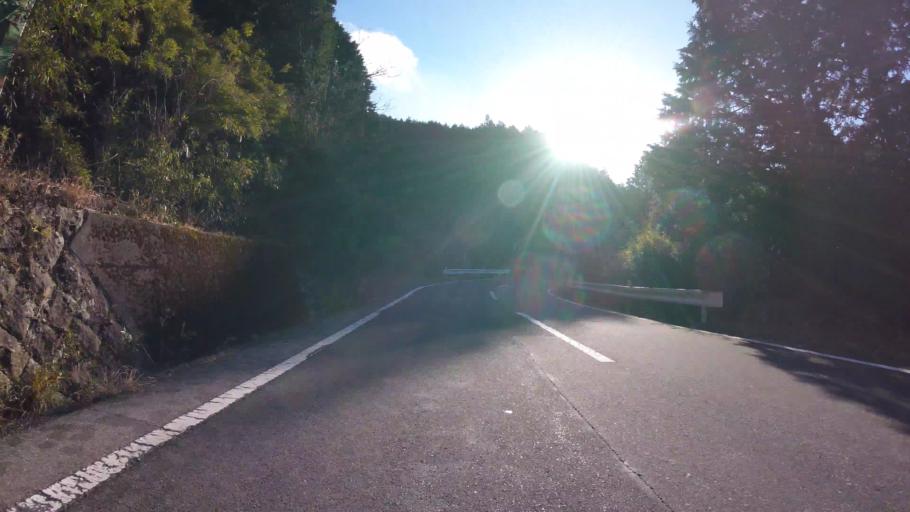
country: JP
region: Kanagawa
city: Yugawara
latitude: 35.1247
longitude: 139.0351
